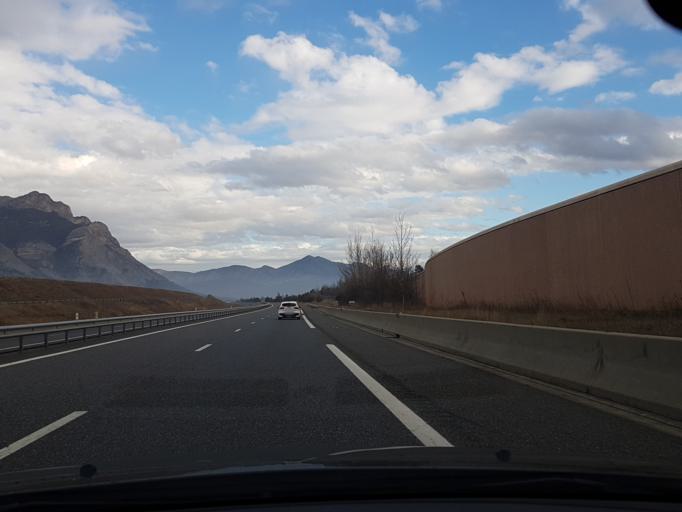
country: FR
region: Provence-Alpes-Cote d'Azur
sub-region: Departement des Hautes-Alpes
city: Laragne-Monteglin
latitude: 44.3703
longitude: 5.9253
